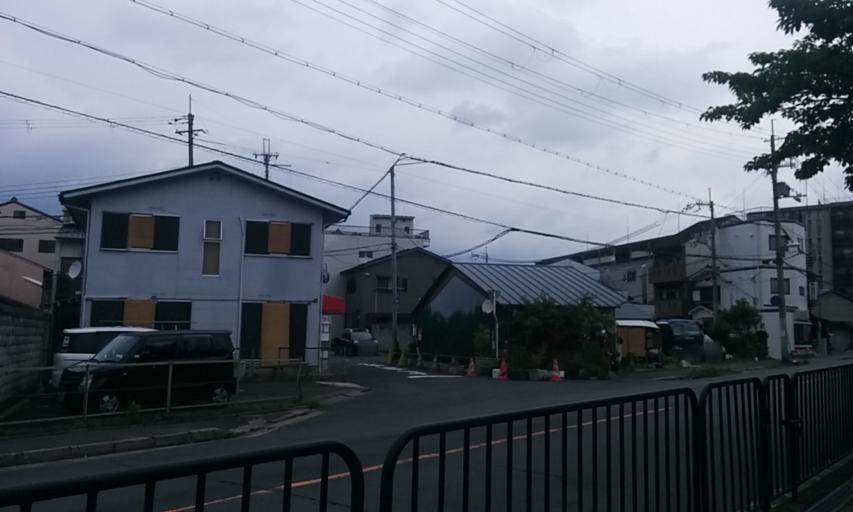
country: JP
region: Kyoto
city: Kyoto
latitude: 34.9851
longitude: 135.7385
